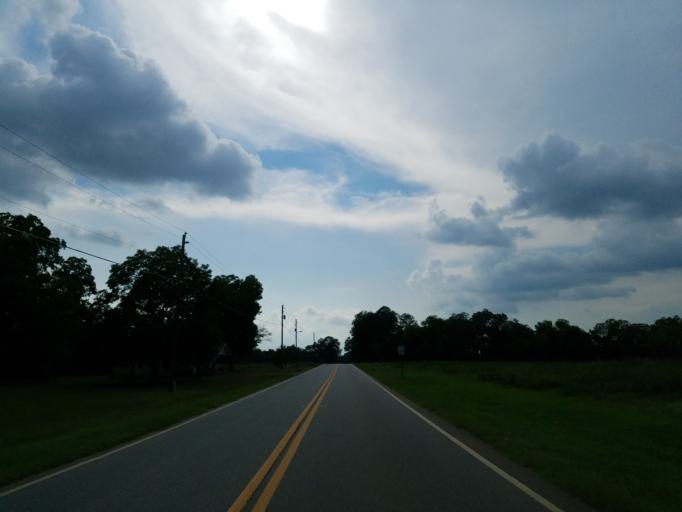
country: US
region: Georgia
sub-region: Dooly County
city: Unadilla
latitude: 32.2604
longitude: -83.7199
